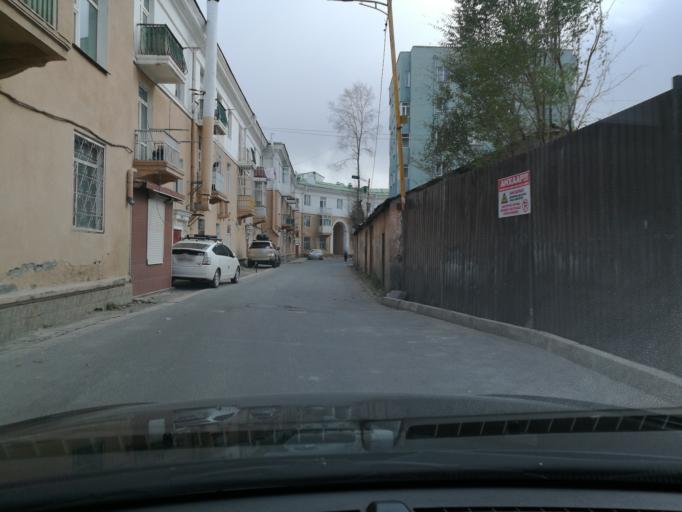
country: MN
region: Ulaanbaatar
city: Ulaanbaatar
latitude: 47.9234
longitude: 106.9176
